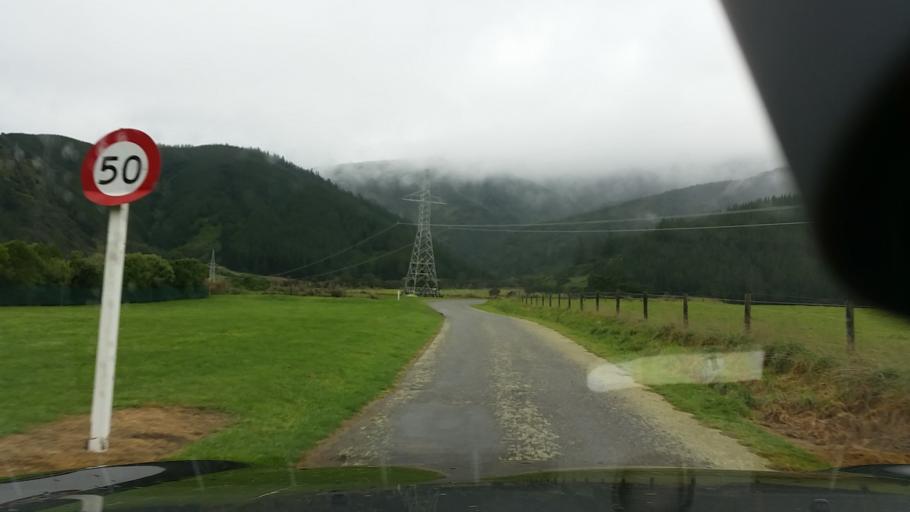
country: NZ
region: Marlborough
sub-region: Marlborough District
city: Picton
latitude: -41.3549
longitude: 174.0745
